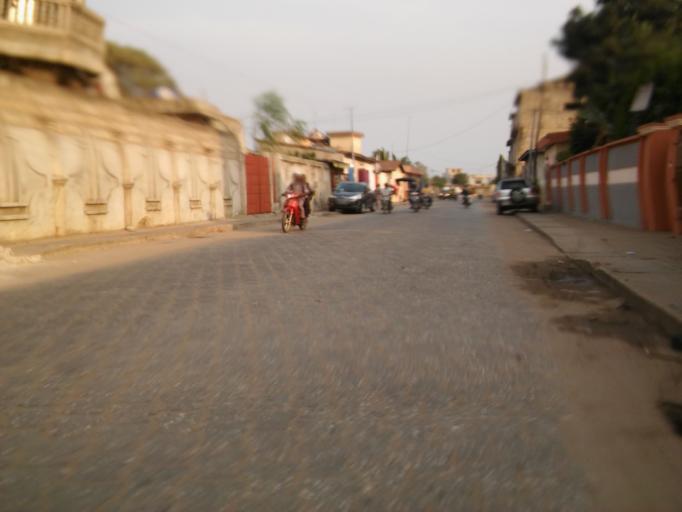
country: BJ
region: Atlantique
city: Abomey-Calavi
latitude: 6.3951
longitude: 2.3507
